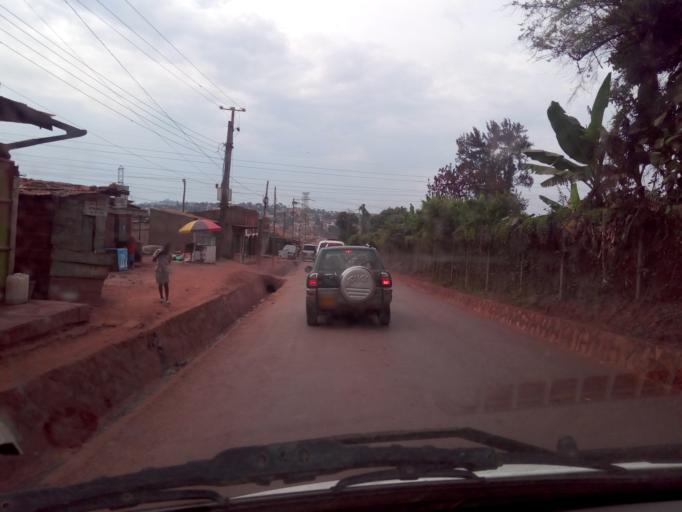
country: UG
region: Central Region
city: Kampala Central Division
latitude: 0.3457
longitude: 32.5774
